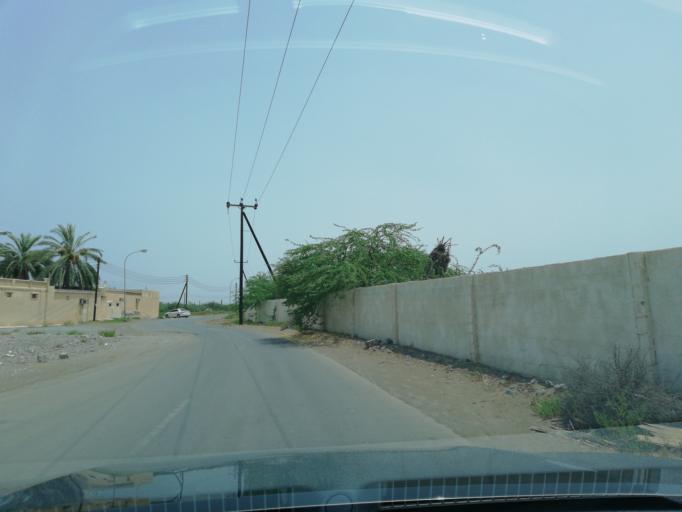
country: OM
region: Al Batinah
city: Al Liwa'
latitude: 24.6129
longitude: 56.5369
